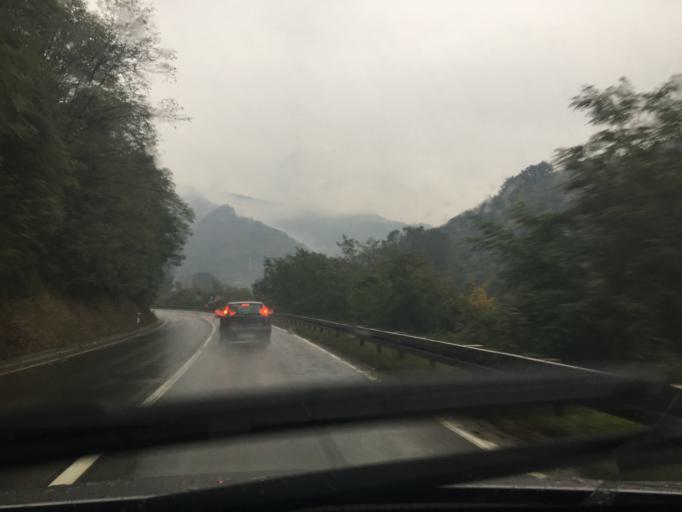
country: RS
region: Central Serbia
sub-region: Pcinjski Okrug
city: Vladicin Han
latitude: 42.7500
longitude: 22.0714
